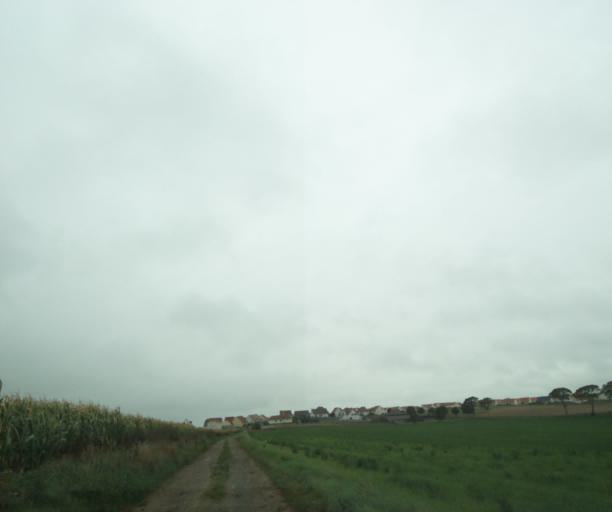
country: FR
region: Nord-Pas-de-Calais
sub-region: Departement du Pas-de-Calais
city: Etaples
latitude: 50.5145
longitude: 1.6618
